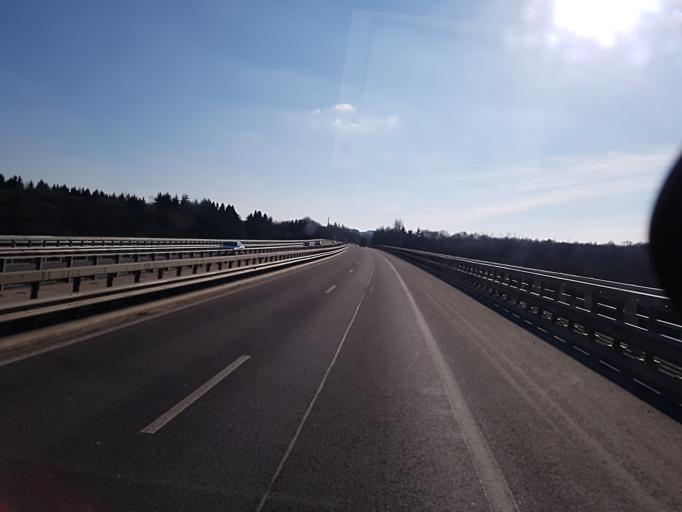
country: DE
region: Rheinland-Pfalz
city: Oberbillig
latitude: 49.7224
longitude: 6.4883
